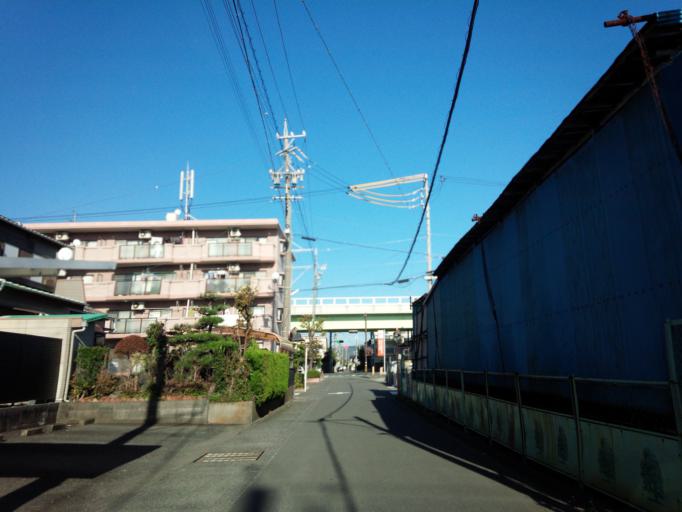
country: JP
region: Shizuoka
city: Shizuoka-shi
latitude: 34.9385
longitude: 138.3965
